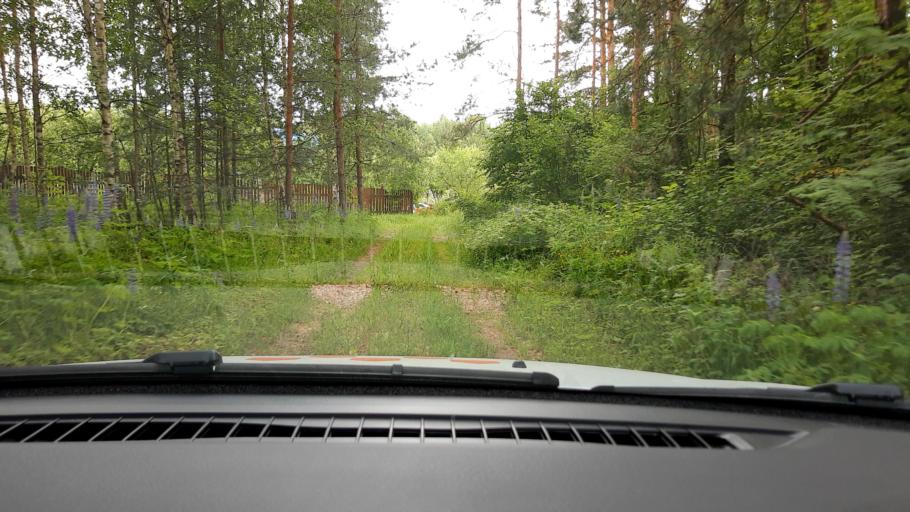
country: RU
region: Nizjnij Novgorod
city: Surovatikha
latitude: 55.8652
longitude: 43.9644
